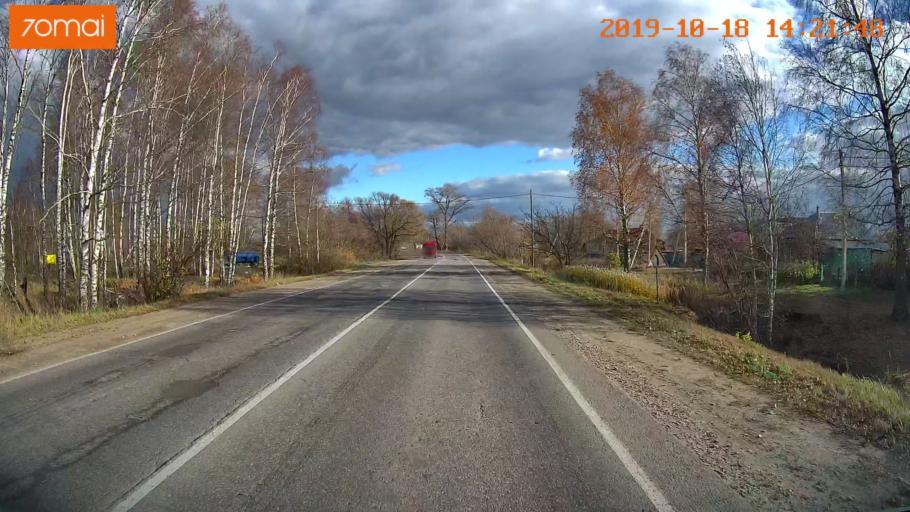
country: RU
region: Rjazan
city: Tuma
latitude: 55.1461
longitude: 40.4637
